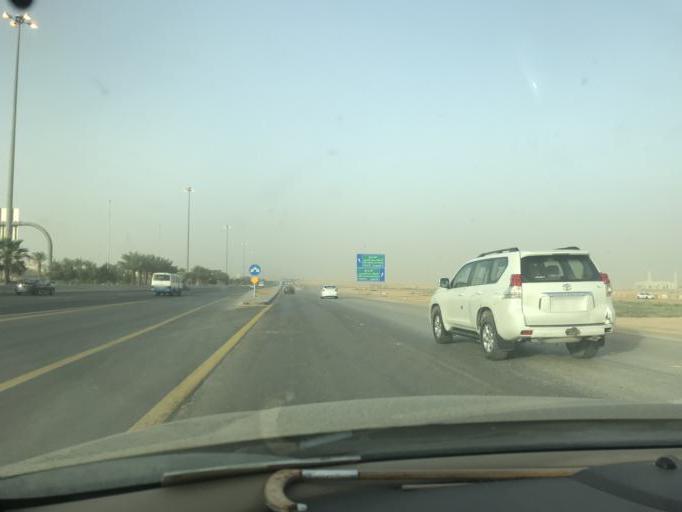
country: SA
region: Ar Riyad
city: Riyadh
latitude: 24.8387
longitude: 46.6421
